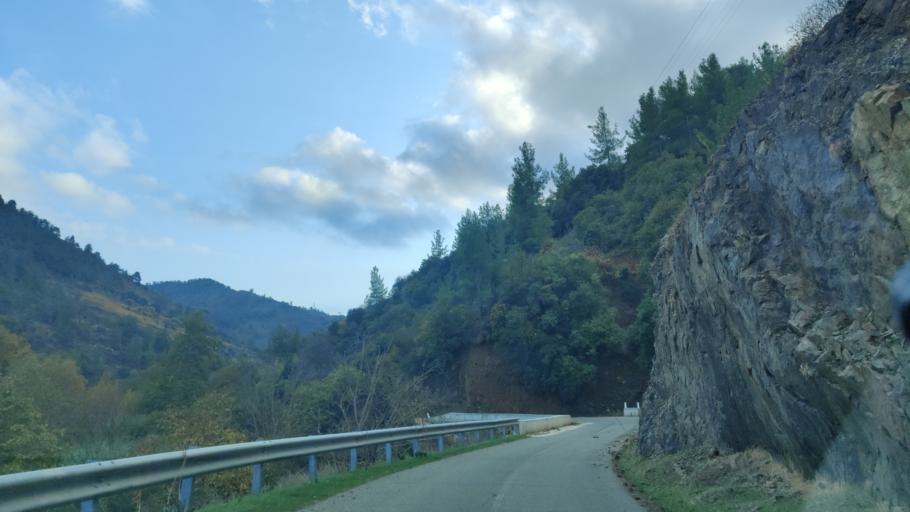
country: CY
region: Lefkosia
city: Lefka
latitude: 35.0513
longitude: 32.7354
